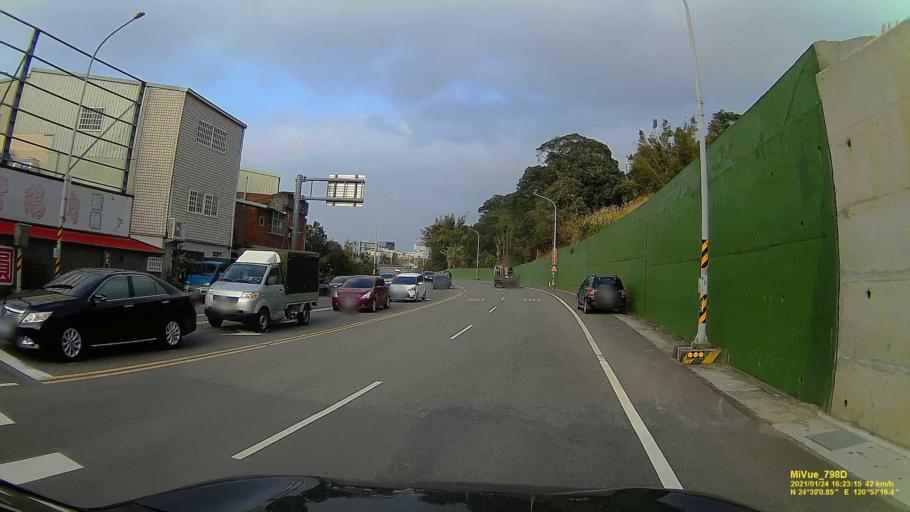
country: TW
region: Taiwan
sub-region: Hsinchu
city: Hsinchu
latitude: 24.6506
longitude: 120.9547
